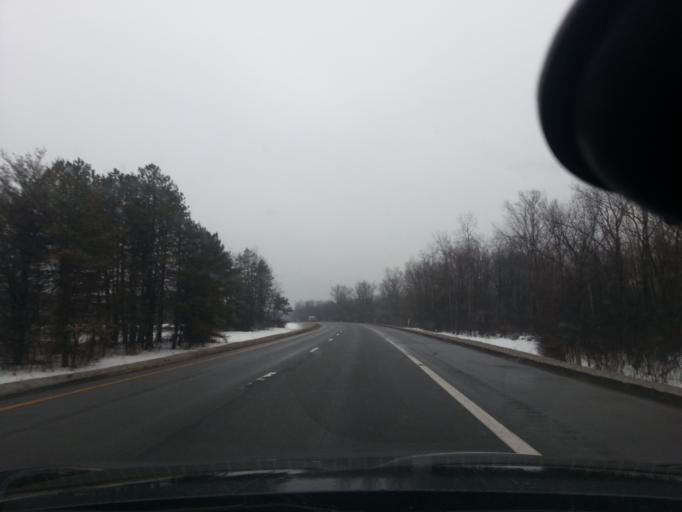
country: US
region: New York
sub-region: Oswego County
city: Pulaski
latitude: 43.6855
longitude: -76.0737
